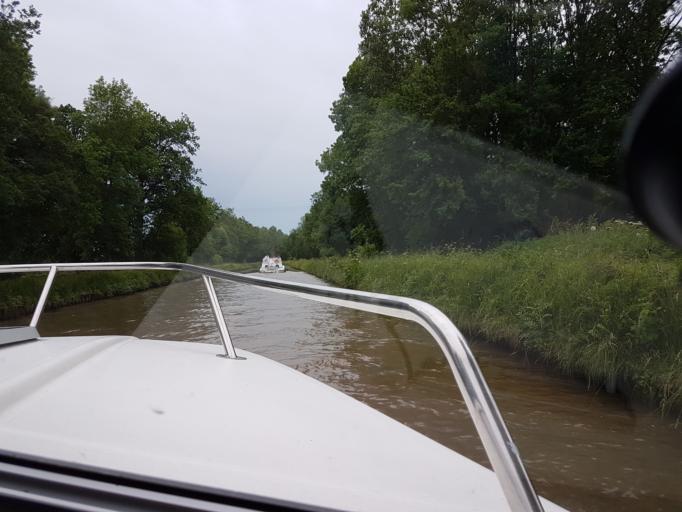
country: FR
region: Bourgogne
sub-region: Departement de la Nievre
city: Clamecy
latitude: 47.3926
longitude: 3.5999
